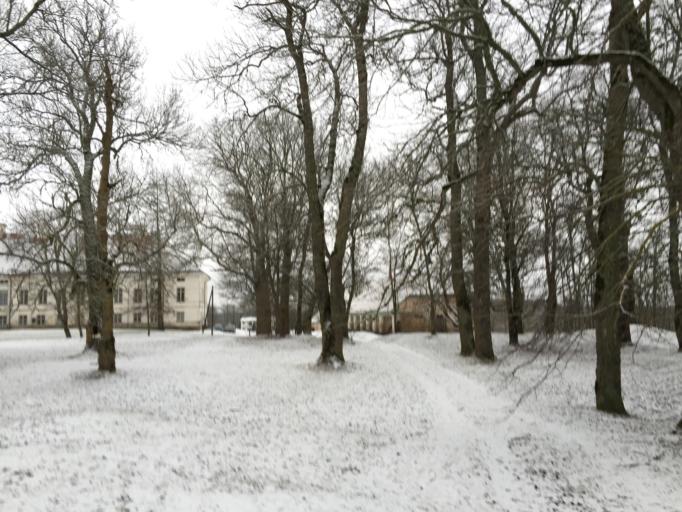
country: EE
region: Laeaene
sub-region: Lihula vald
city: Lihula
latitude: 58.6943
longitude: 23.8384
